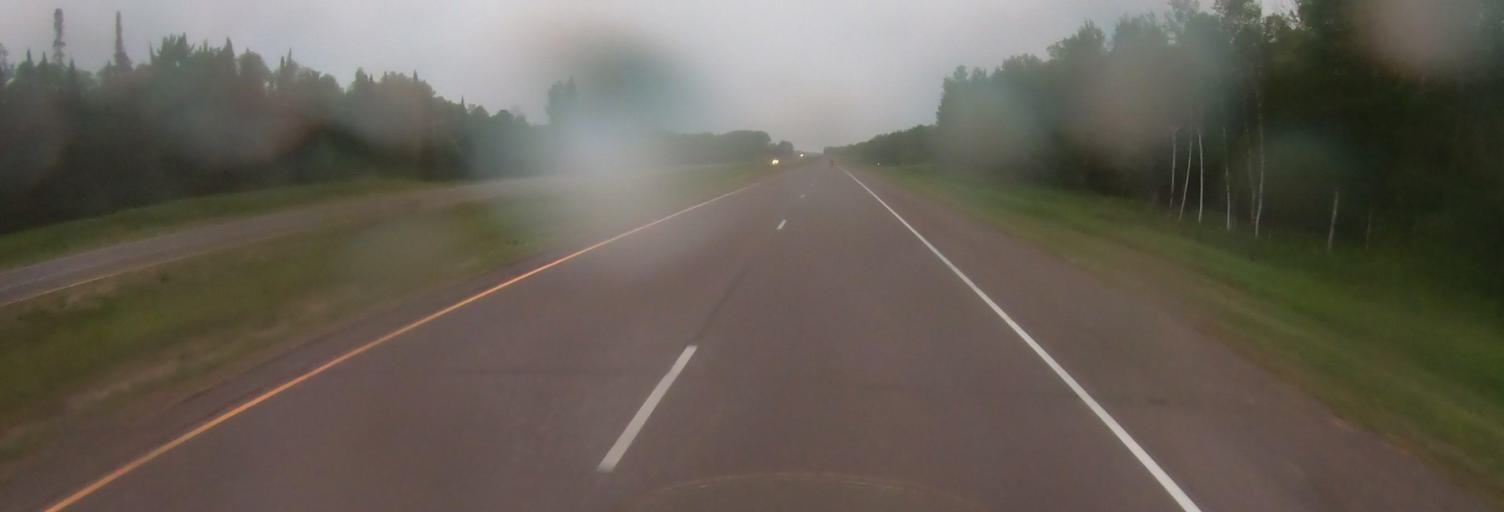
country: US
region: Minnesota
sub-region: Carlton County
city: Cloquet
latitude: 46.9025
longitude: -92.4701
